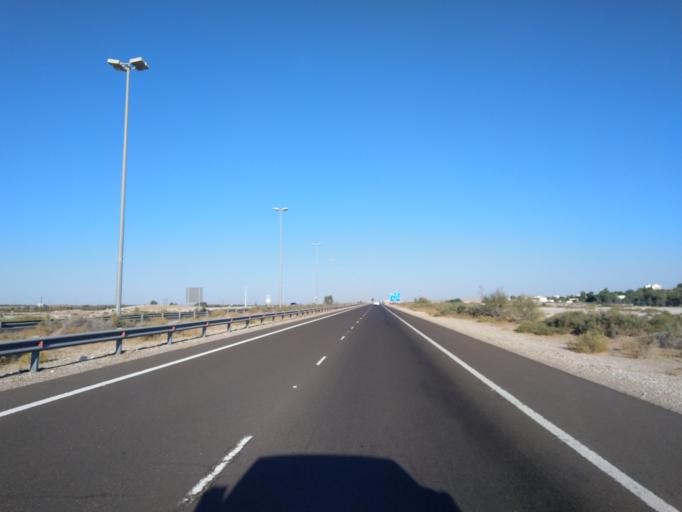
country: OM
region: Al Buraimi
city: Al Buraymi
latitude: 24.5238
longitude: 55.5414
